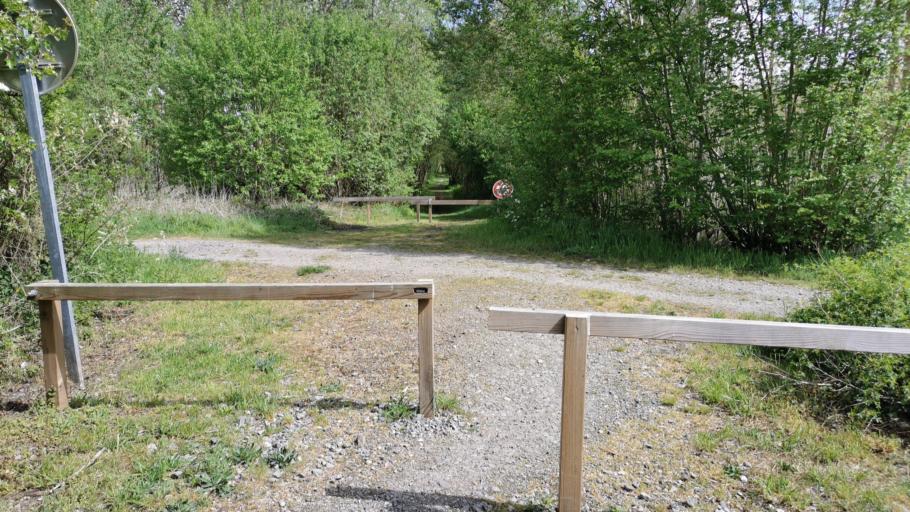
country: FR
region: Picardie
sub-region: Departement de la Somme
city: Doingt
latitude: 49.9249
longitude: 3.0174
